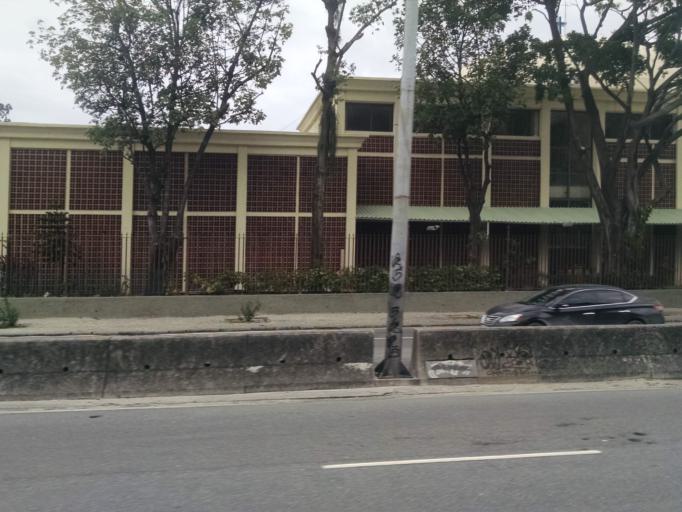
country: BR
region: Rio de Janeiro
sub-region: Rio De Janeiro
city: Rio de Janeiro
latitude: -23.0080
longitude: -43.3038
